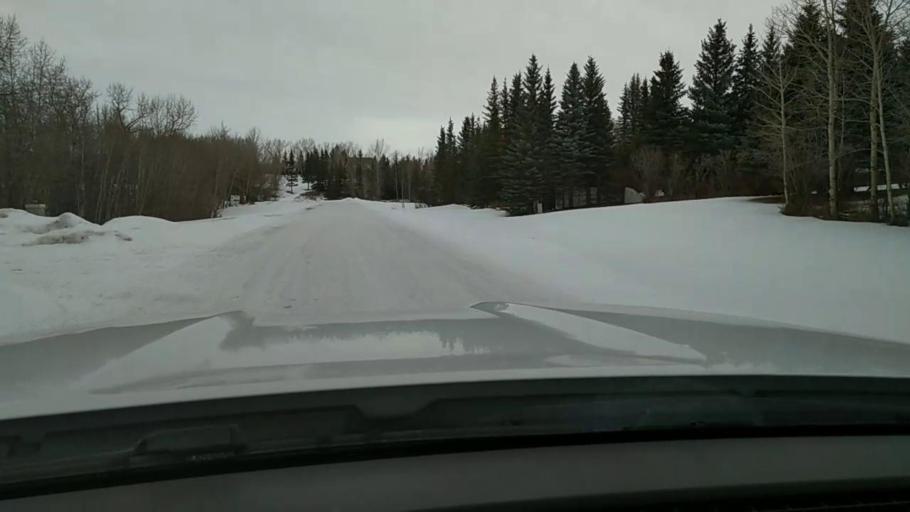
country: CA
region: Alberta
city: Calgary
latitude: 51.1574
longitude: -114.2555
